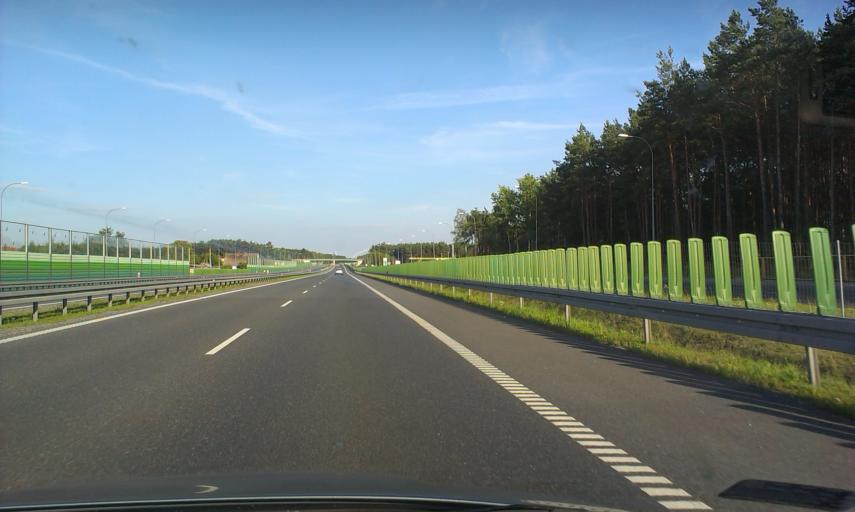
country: PL
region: Kujawsko-Pomorskie
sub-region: Powiat bydgoski
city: Biale Blota
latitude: 53.0683
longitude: 17.9328
